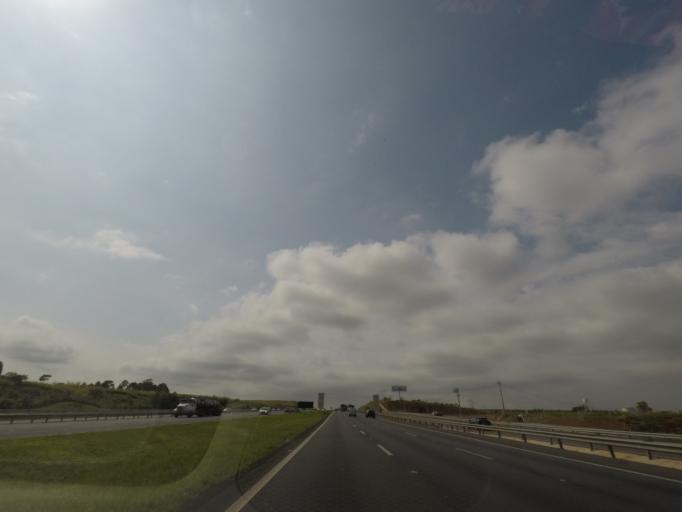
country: BR
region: Sao Paulo
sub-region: Campinas
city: Campinas
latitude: -22.8689
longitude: -47.0194
